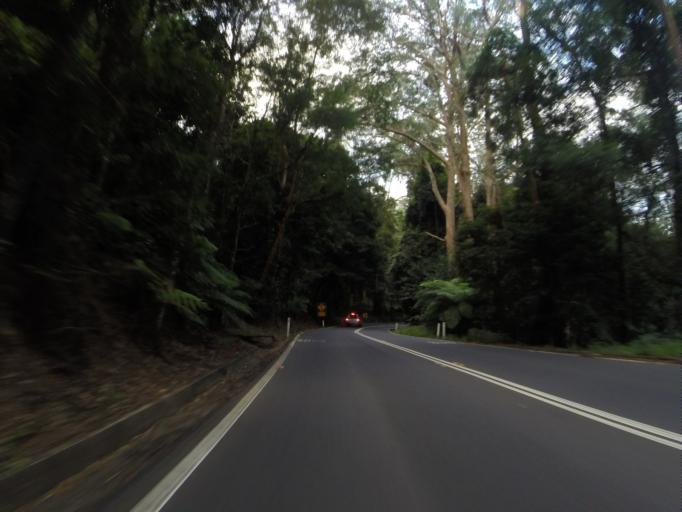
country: AU
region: New South Wales
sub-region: Shellharbour
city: Calderwood
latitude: -34.5569
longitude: 150.6475
